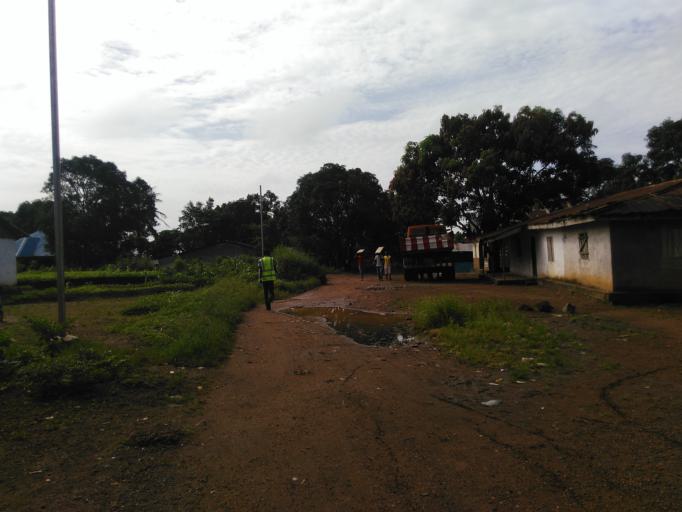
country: SL
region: Southern Province
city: Rotifunk
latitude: 8.4875
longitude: -12.7563
